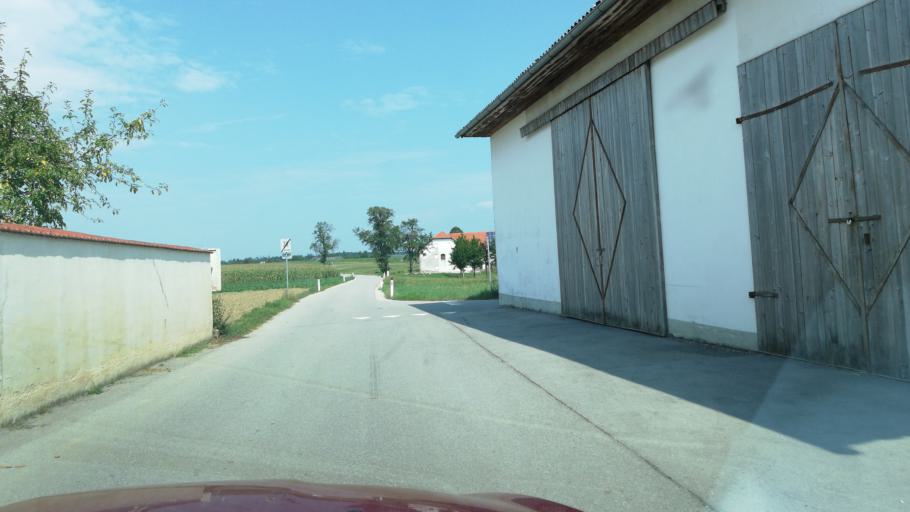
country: AT
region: Upper Austria
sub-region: Politischer Bezirk Steyr-Land
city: Sierning
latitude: 48.0512
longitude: 14.3074
